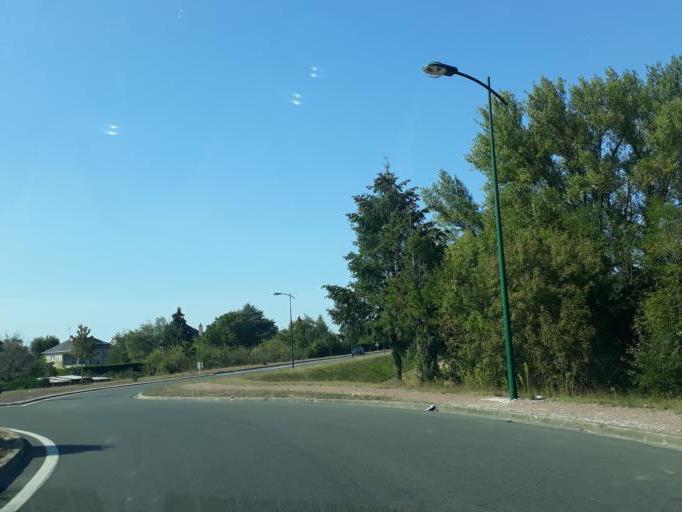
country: FR
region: Centre
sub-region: Departement du Loir-et-Cher
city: Selles-sur-Cher
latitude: 47.2734
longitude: 1.5598
